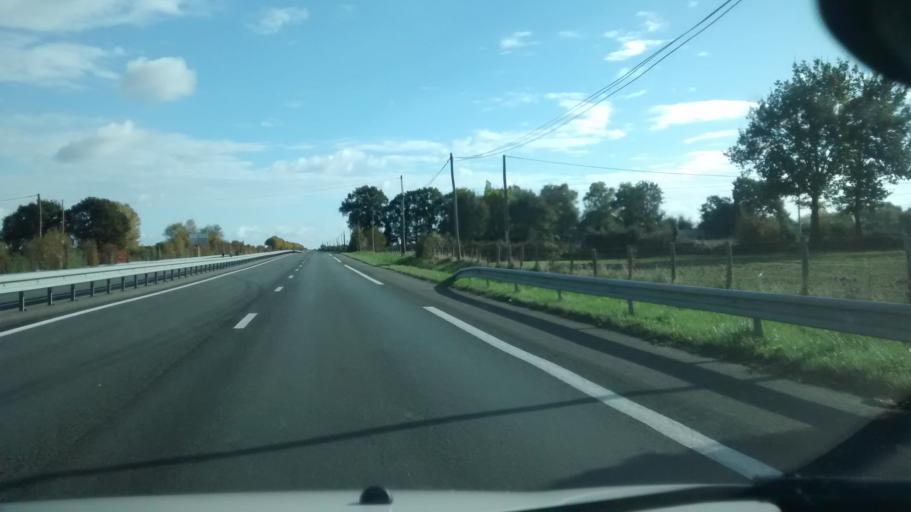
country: FR
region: Pays de la Loire
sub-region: Departement de Maine-et-Loire
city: Pouance
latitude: 47.7350
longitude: -1.1407
